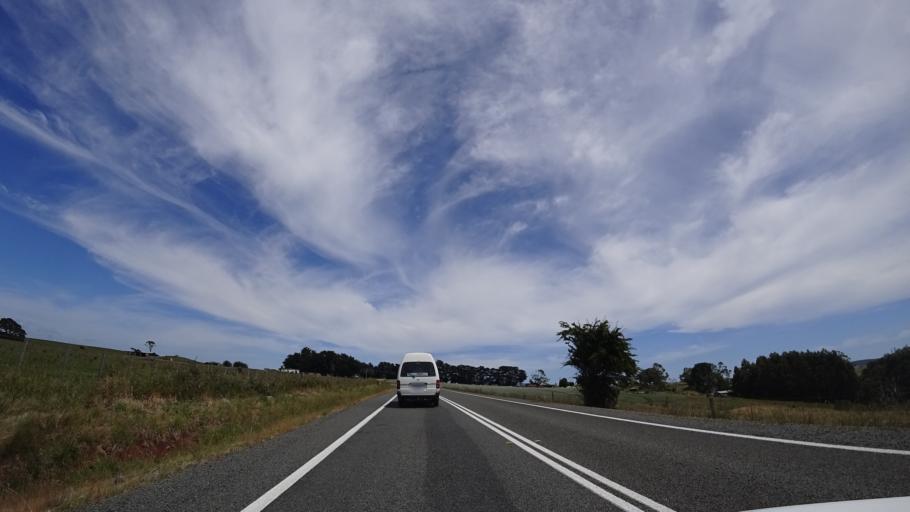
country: AU
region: Tasmania
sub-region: Dorset
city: Scottsdale
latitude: -41.1095
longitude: 147.8663
